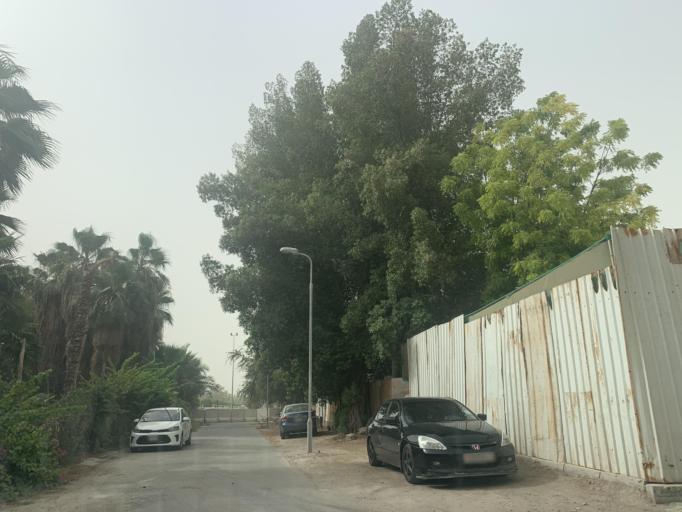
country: BH
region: Manama
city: Jidd Hafs
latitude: 26.2237
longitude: 50.5579
